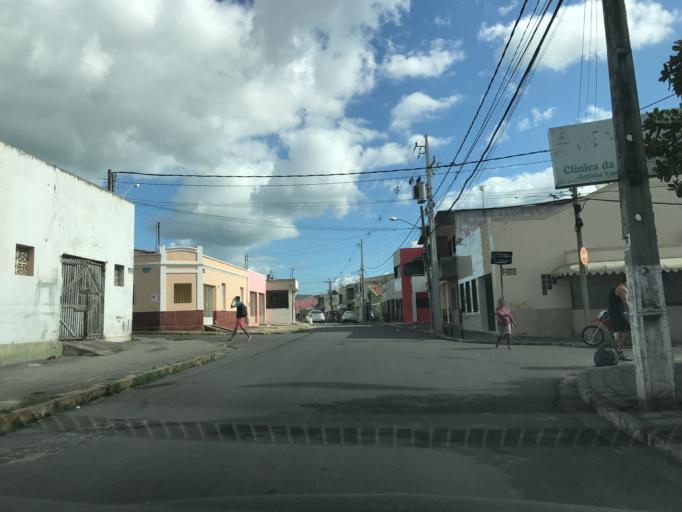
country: BR
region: Pernambuco
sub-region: Bezerros
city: Bezerros
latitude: -8.2387
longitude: -35.7537
